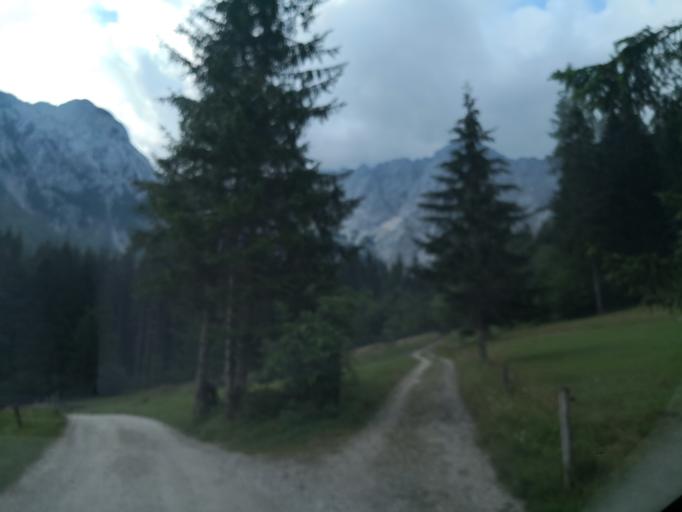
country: SI
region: Jezersko
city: Zgornje Jezersko
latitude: 46.3895
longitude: 14.5312
